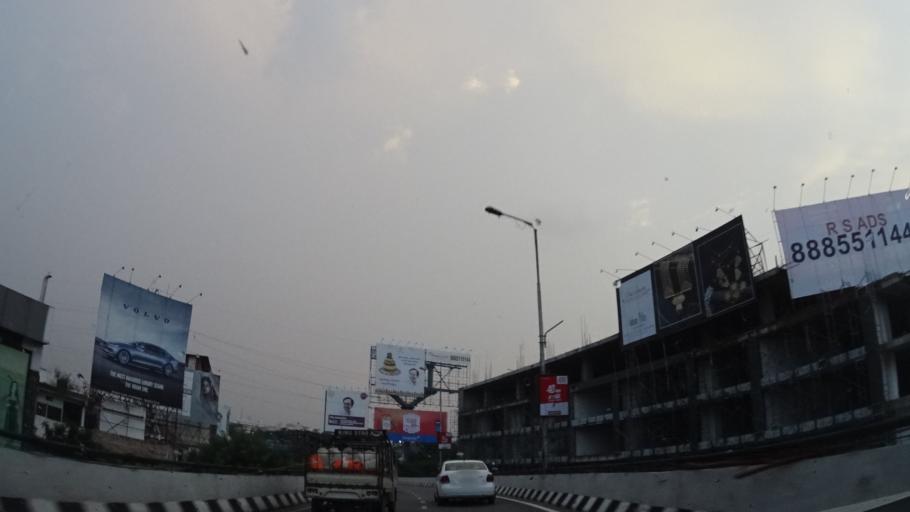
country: IN
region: Telangana
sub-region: Hyderabad
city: Hyderabad
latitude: 17.4256
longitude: 78.4489
